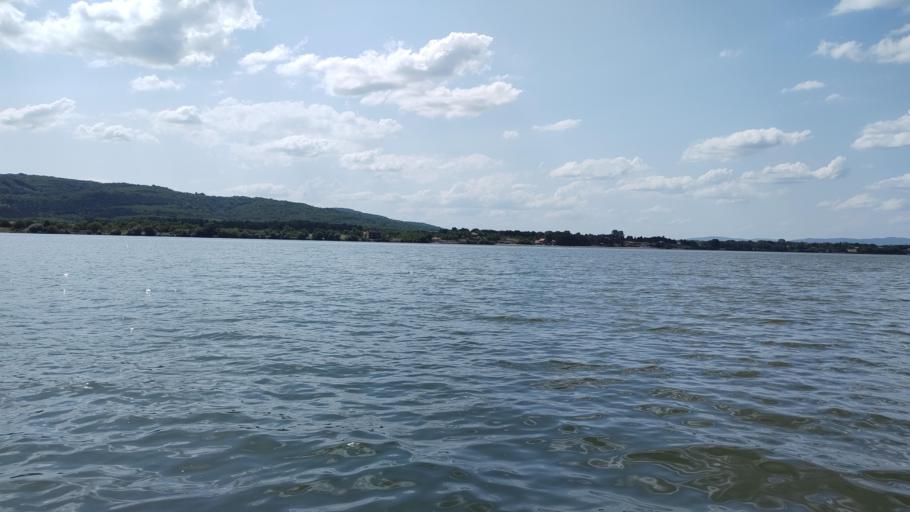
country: RS
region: Central Serbia
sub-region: Branicevski Okrug
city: Golubac
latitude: 44.6733
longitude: 21.6183
